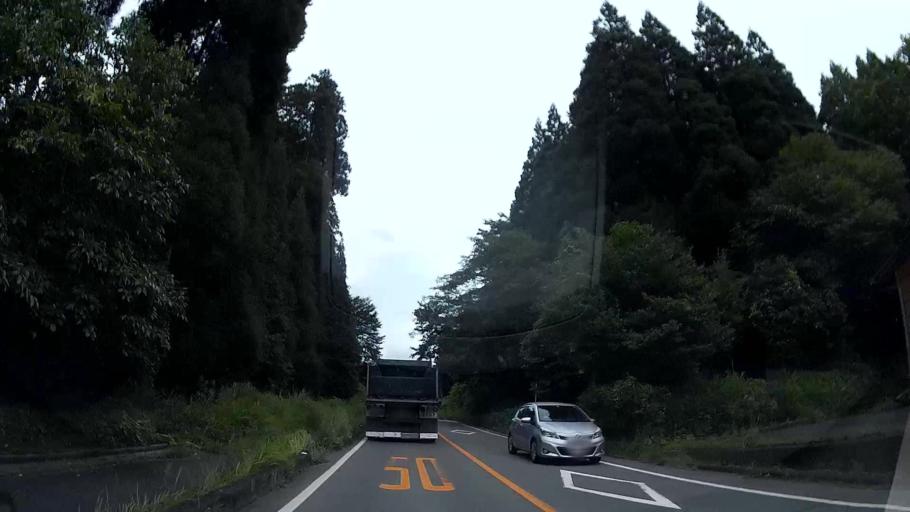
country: JP
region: Oita
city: Tsukawaki
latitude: 33.1252
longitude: 131.0550
